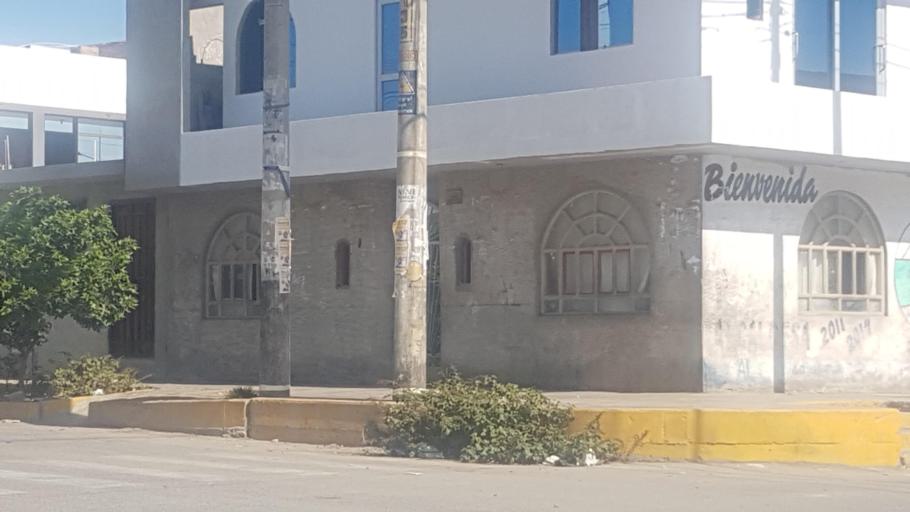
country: PE
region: Ancash
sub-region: Provincia de Santa
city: Chimbote
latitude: -9.0932
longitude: -78.5727
